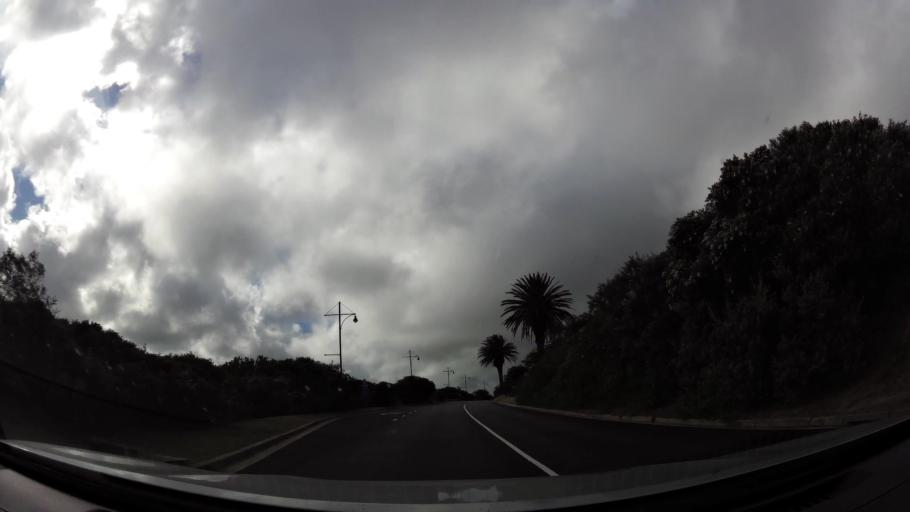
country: ZA
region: Western Cape
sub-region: Eden District Municipality
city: Knysna
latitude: -34.0694
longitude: 23.0887
